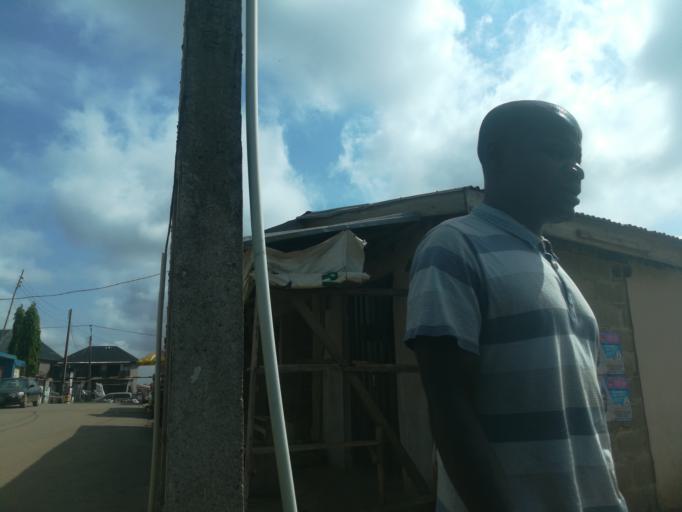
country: NG
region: Oyo
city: Ibadan
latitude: 7.3341
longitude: 3.8565
